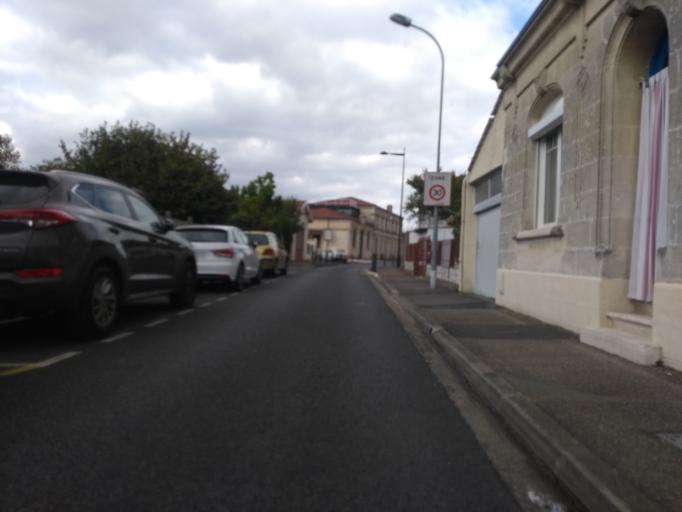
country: FR
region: Aquitaine
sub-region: Departement de la Gironde
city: Begles
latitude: 44.8072
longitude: -0.5668
